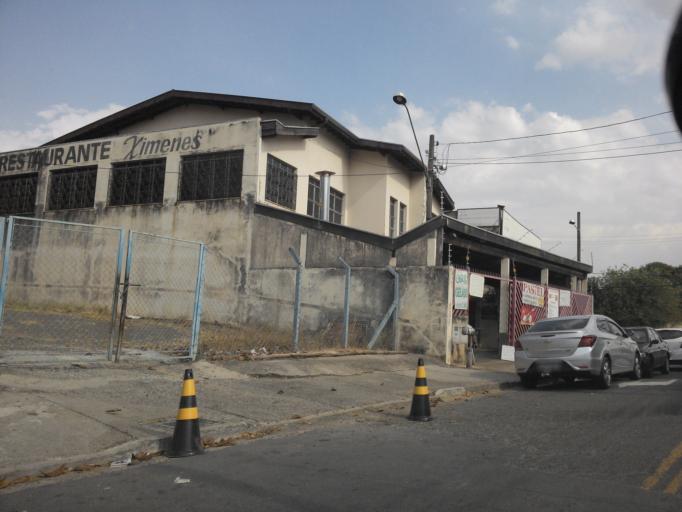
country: BR
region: Sao Paulo
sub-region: Campinas
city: Campinas
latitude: -22.8971
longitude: -47.0959
